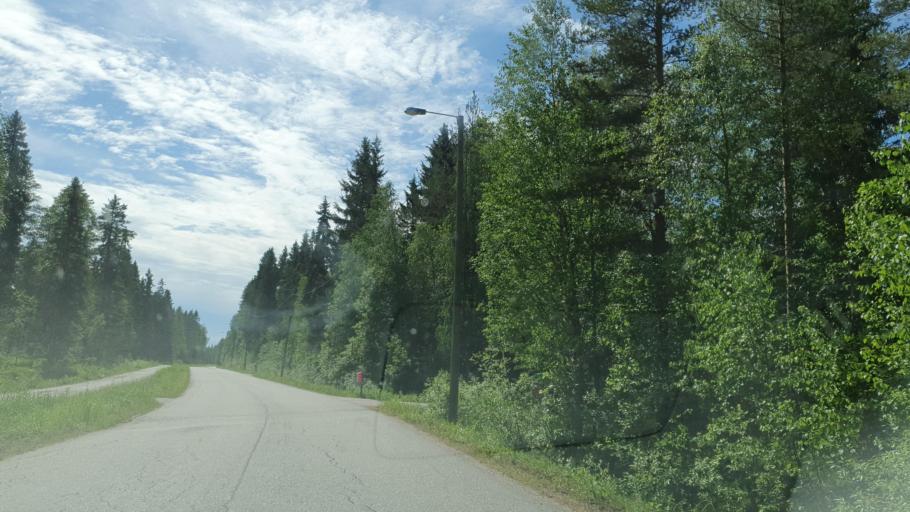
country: FI
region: Kainuu
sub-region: Kehys-Kainuu
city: Hyrynsalmi
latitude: 64.6863
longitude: 28.4665
